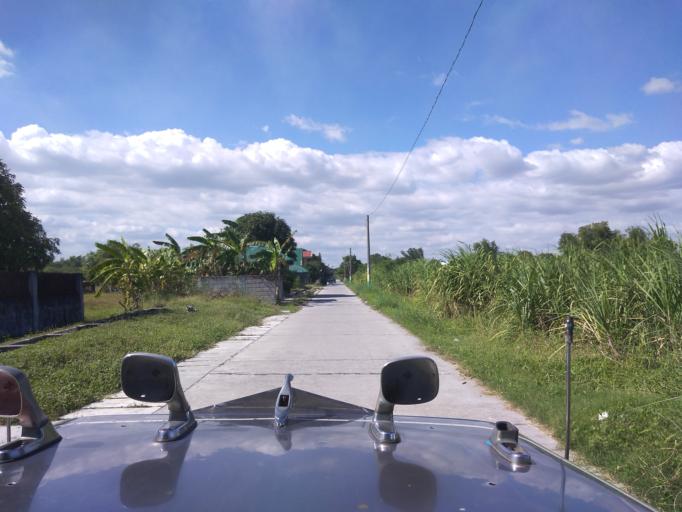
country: PH
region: Central Luzon
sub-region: Province of Pampanga
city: Bacolor
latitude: 15.0263
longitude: 120.6336
